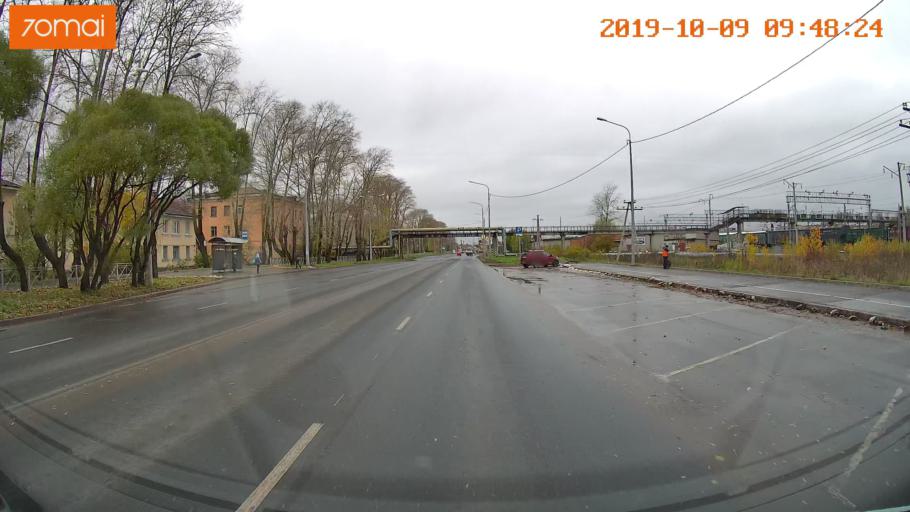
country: RU
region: Vologda
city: Vologda
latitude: 59.1943
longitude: 39.9292
